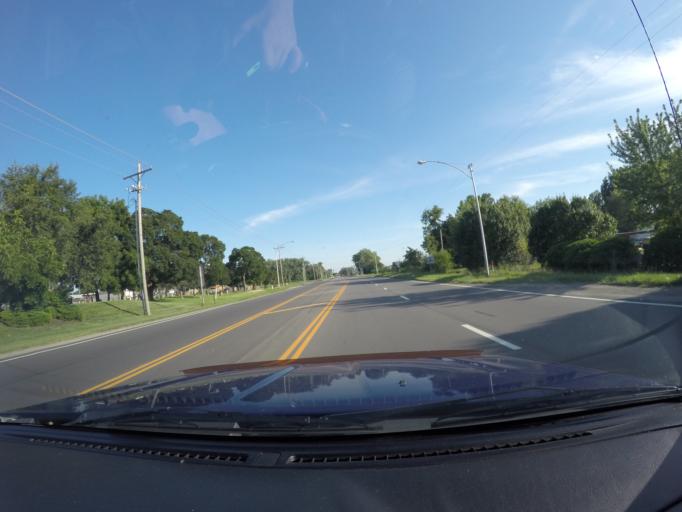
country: US
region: Kansas
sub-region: Douglas County
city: Lawrence
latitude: 39.0027
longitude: -95.2335
